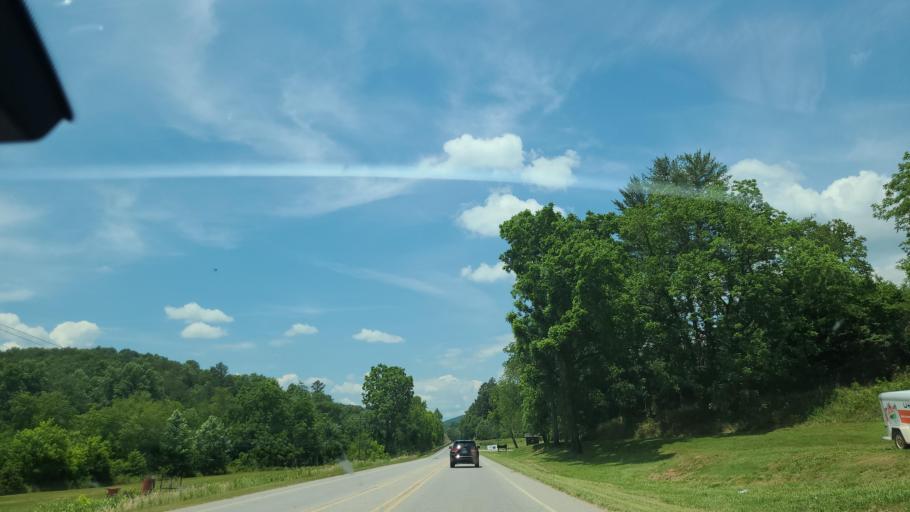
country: US
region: North Carolina
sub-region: Clay County
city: Hayesville
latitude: 35.0393
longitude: -83.8740
